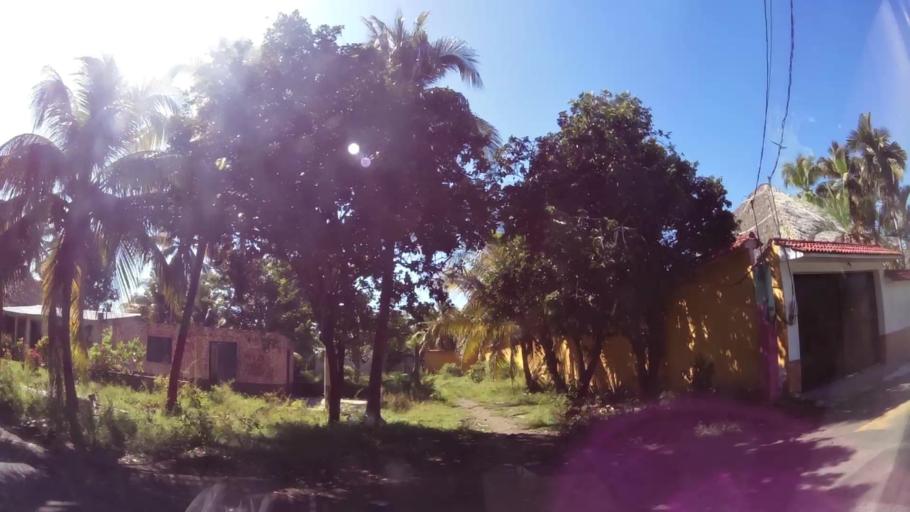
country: GT
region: Escuintla
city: Iztapa
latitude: 13.9178
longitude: -90.5535
